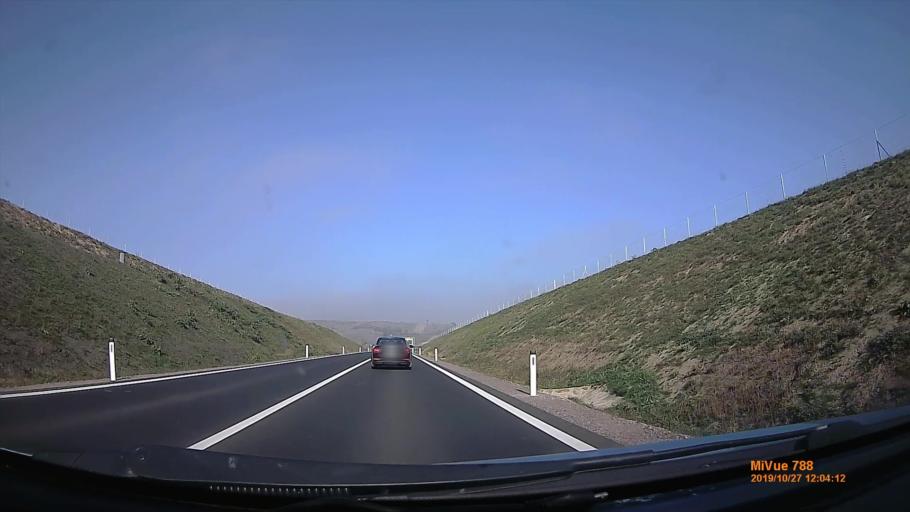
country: AT
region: Lower Austria
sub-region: Politischer Bezirk Mistelbach
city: Drasenhofen
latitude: 48.7515
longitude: 16.6357
